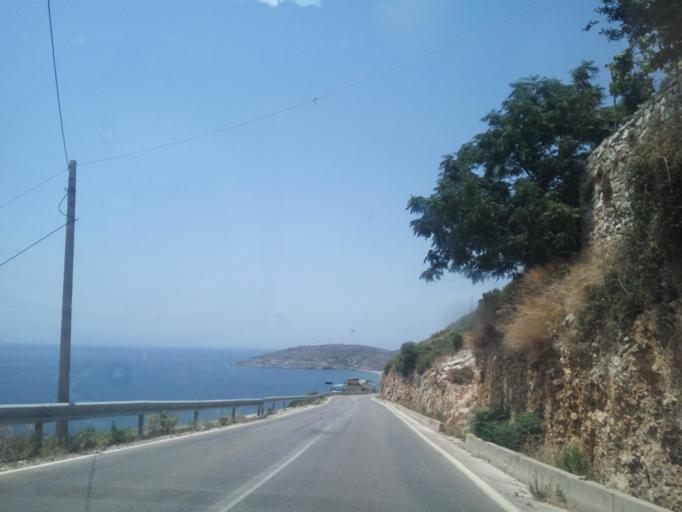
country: AL
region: Vlore
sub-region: Rrethi i Sarandes
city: Lukove
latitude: 40.0525
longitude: 19.8358
